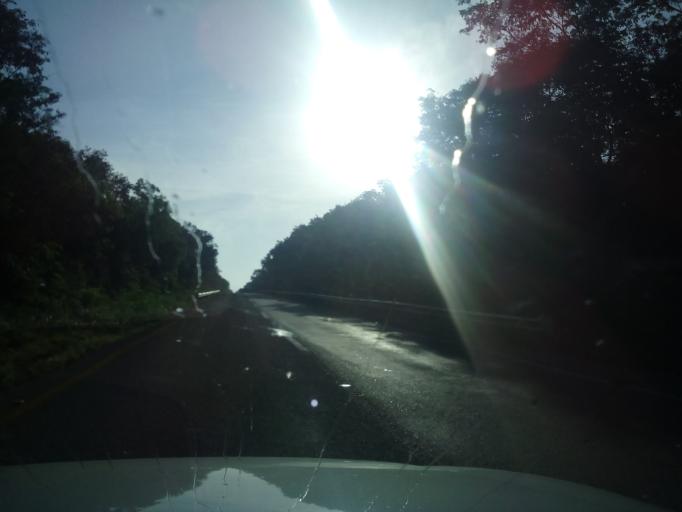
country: MX
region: Yucatan
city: Piste
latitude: 20.7431
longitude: -88.6760
